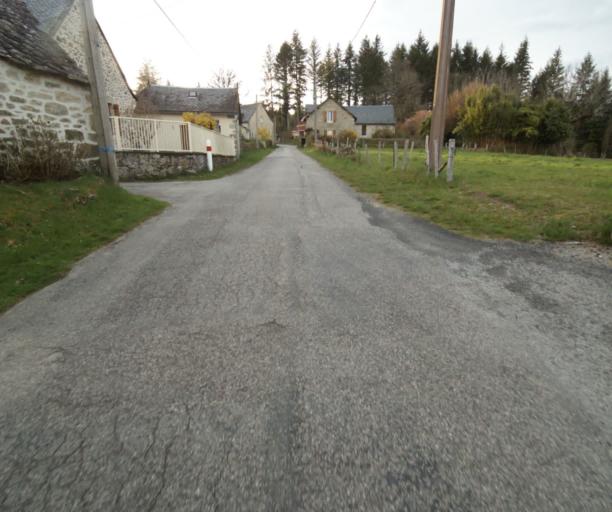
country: FR
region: Limousin
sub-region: Departement de la Correze
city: Argentat
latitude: 45.2205
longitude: 1.9694
